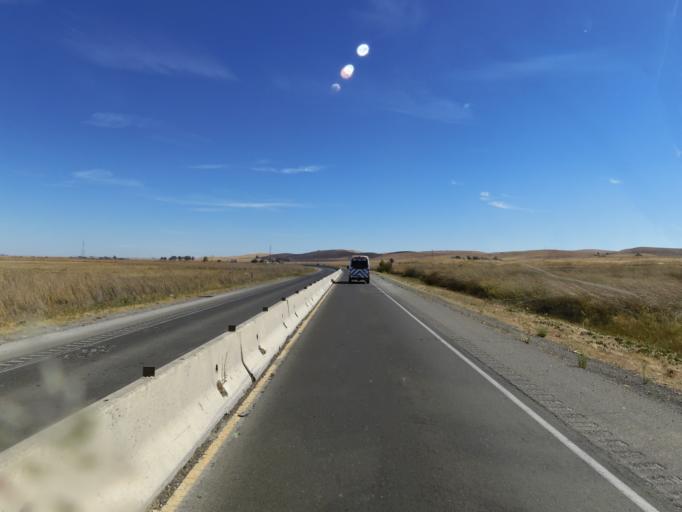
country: US
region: California
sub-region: Solano County
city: Suisun
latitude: 38.2317
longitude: -121.9793
